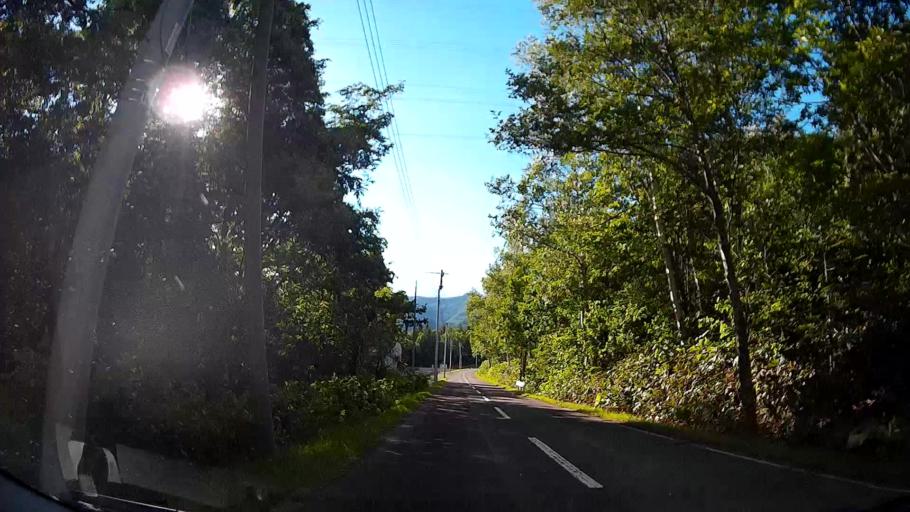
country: JP
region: Hokkaido
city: Sapporo
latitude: 42.9848
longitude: 141.1236
